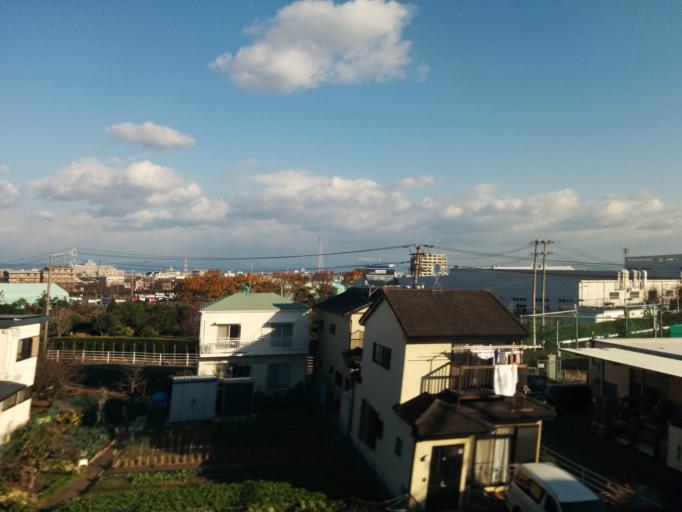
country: JP
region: Shizuoka
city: Hamamatsu
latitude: 34.7088
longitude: 137.7690
